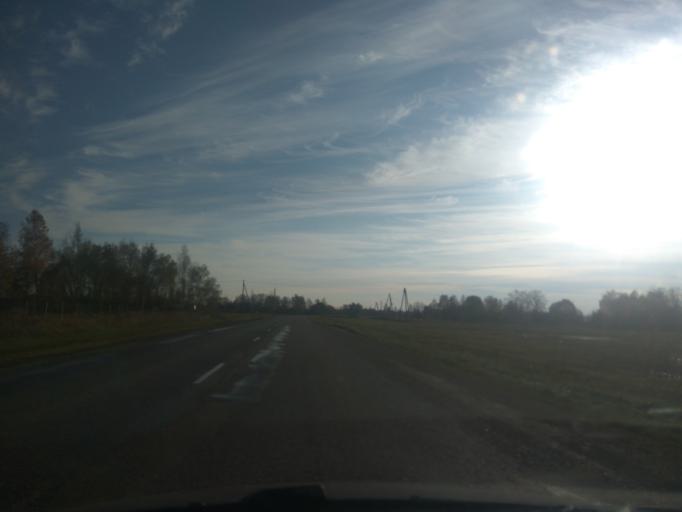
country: LV
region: Ventspils
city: Ventspils
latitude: 57.3284
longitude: 21.5641
